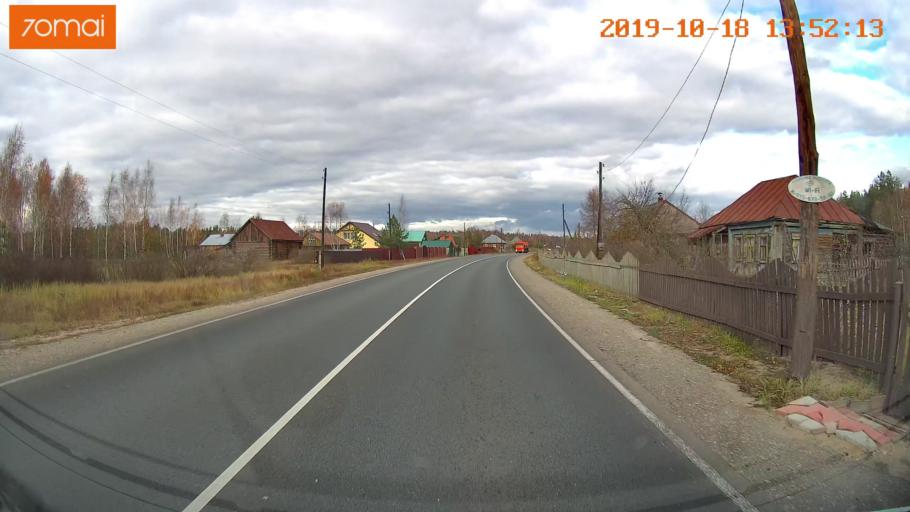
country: RU
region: Moskovskaya
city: Radovitskiy
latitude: 55.0275
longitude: 39.9664
